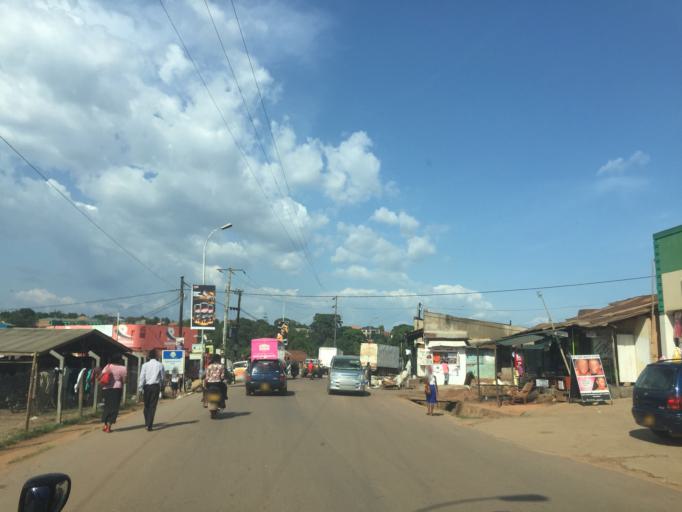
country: UG
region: Central Region
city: Kampala Central Division
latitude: 0.3818
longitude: 32.5602
